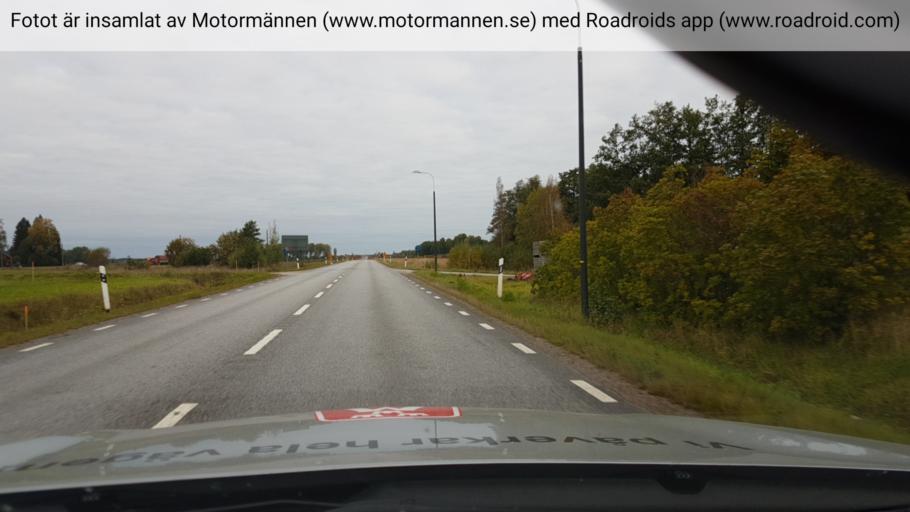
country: SE
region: Uppsala
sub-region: Tierps Kommun
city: Tierp
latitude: 60.3332
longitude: 17.5096
